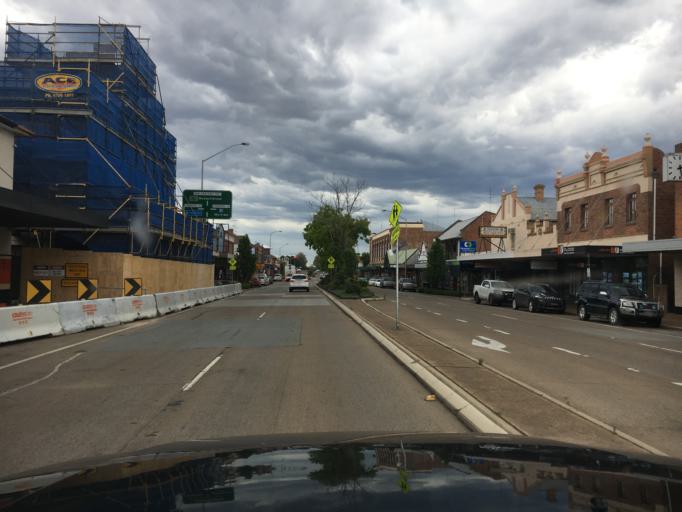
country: AU
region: New South Wales
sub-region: Muswellbrook
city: Muswellbrook
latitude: -32.0489
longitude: 150.8679
